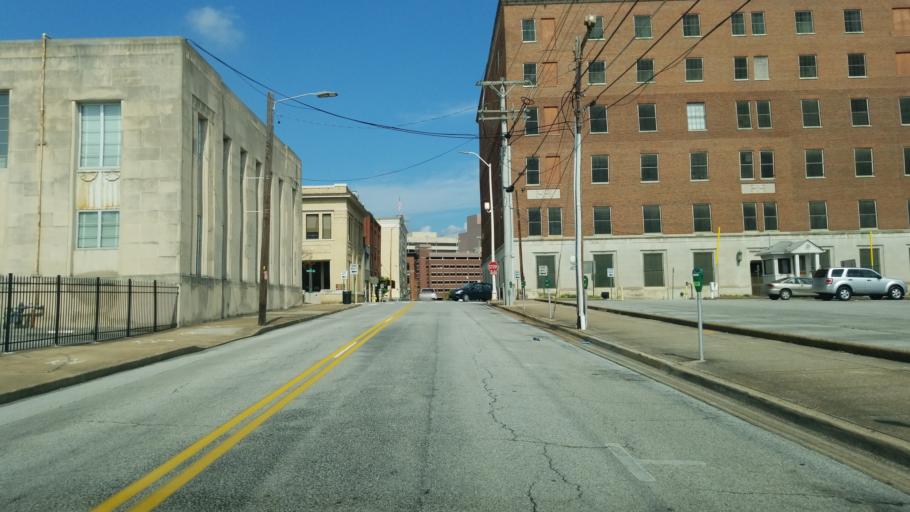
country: US
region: Tennessee
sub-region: Hamilton County
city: Chattanooga
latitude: 35.0440
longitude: -85.3069
